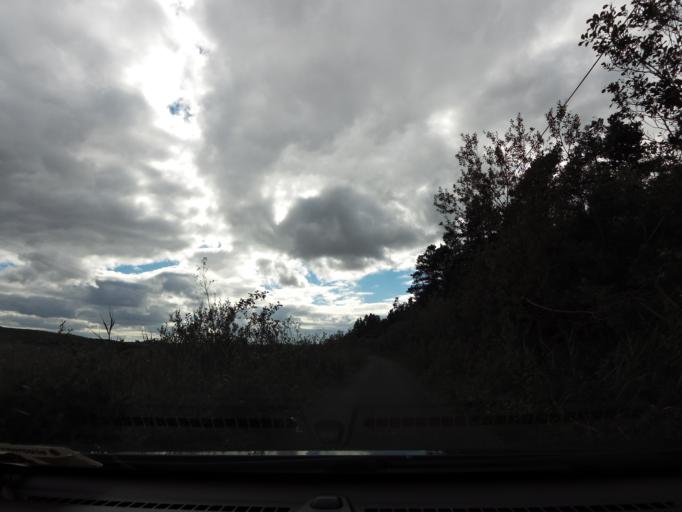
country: IE
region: Connaught
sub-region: County Galway
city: Moycullen
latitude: 53.3234
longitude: -9.1248
